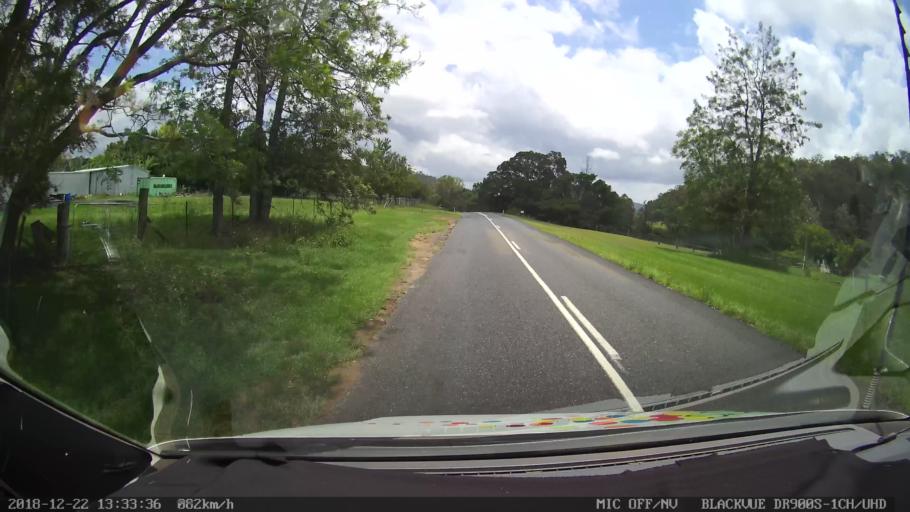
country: AU
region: New South Wales
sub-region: Clarence Valley
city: Coutts Crossing
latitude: -29.8633
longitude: 152.8255
